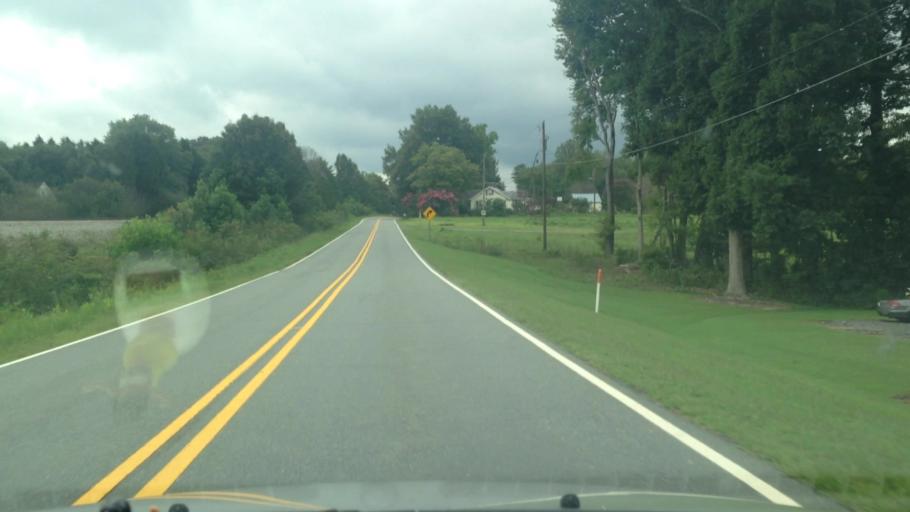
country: US
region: North Carolina
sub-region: Stokes County
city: Walnut Cove
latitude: 36.2441
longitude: -80.1535
